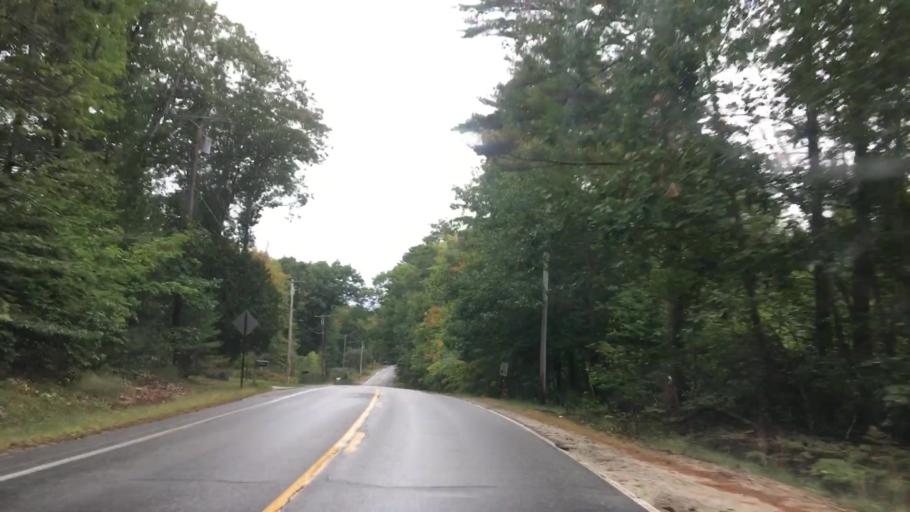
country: US
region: Maine
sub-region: Cumberland County
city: Raymond
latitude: 43.9640
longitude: -70.4652
